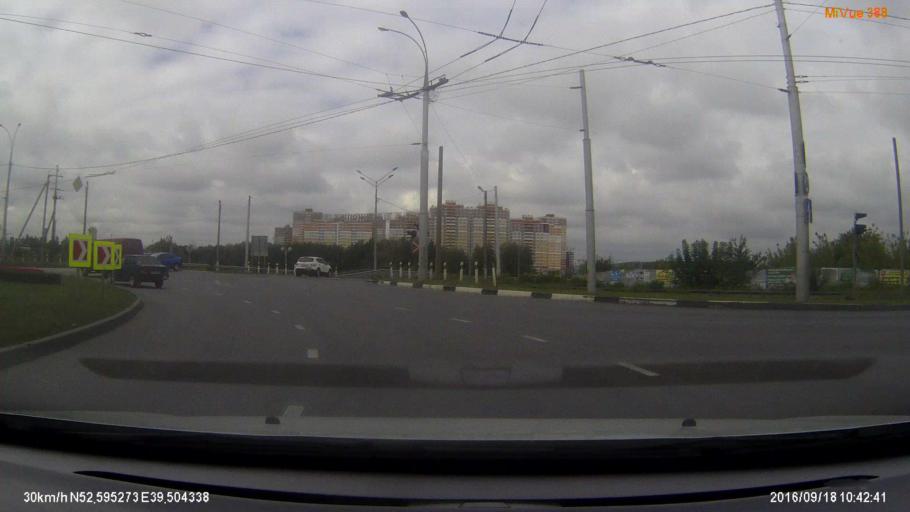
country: RU
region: Lipetsk
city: Syrskoye
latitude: 52.5950
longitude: 39.5044
